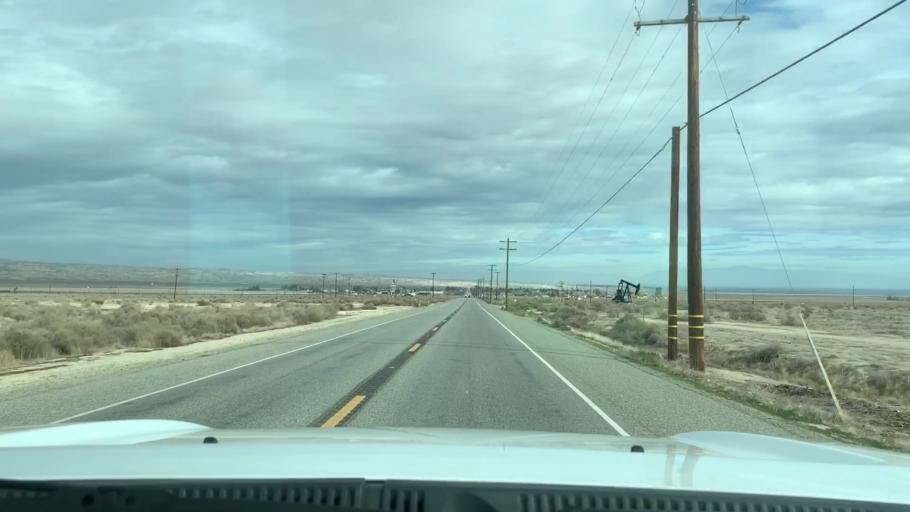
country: US
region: California
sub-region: Kern County
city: Ford City
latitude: 35.1947
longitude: -119.4273
